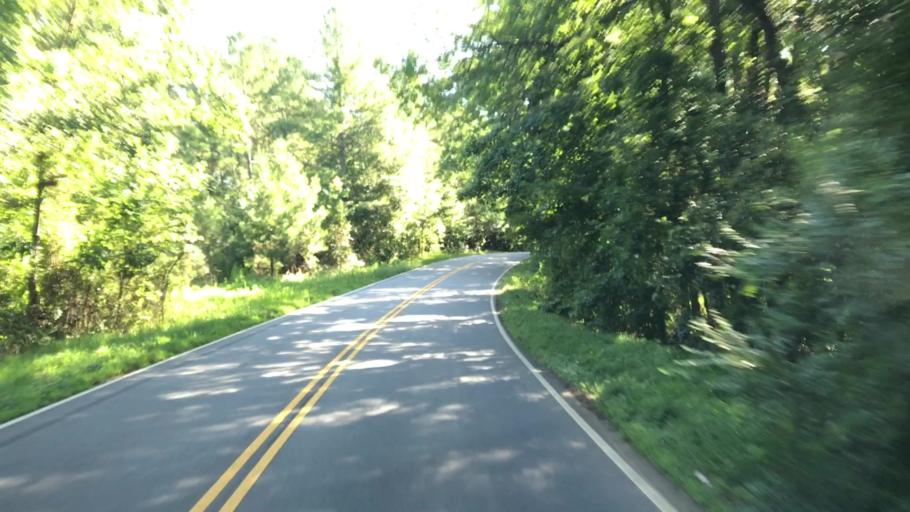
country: US
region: South Carolina
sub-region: Anderson County
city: Williamston
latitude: 34.6360
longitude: -82.4627
